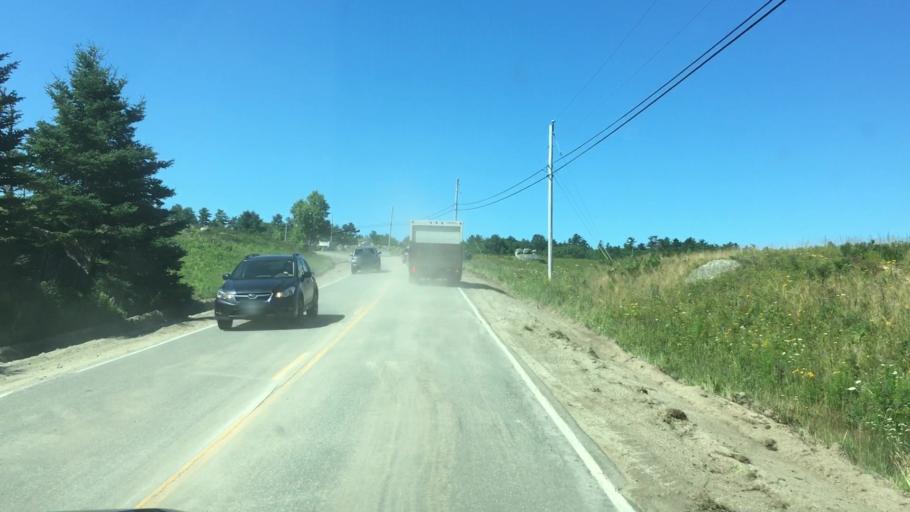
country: US
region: Maine
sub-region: Hancock County
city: Sedgwick
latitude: 44.3549
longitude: -68.5840
